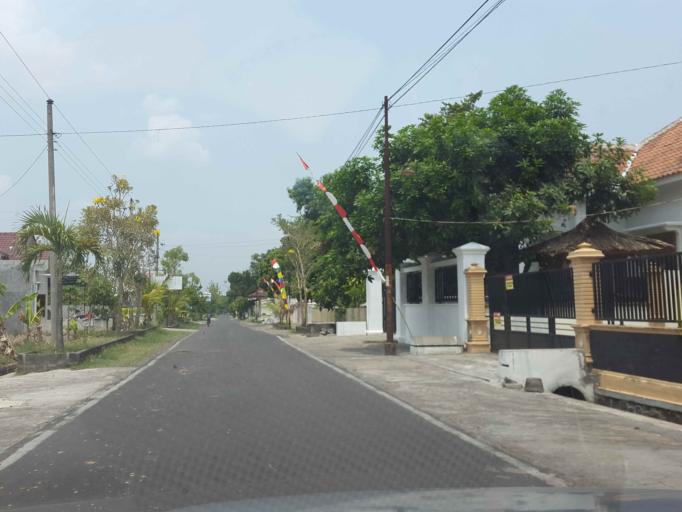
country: ID
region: Central Java
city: Jaten
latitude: -7.5822
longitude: 110.9331
